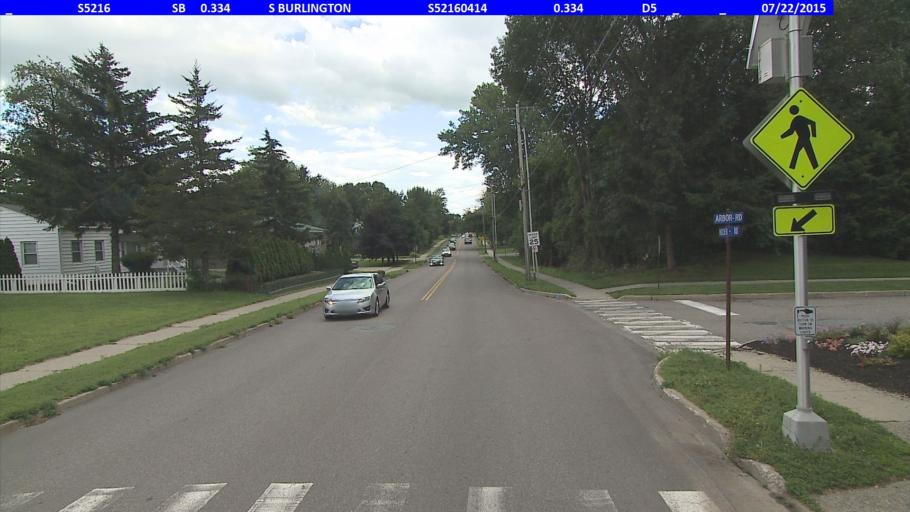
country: US
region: Vermont
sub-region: Chittenden County
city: South Burlington
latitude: 44.4717
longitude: -73.1723
